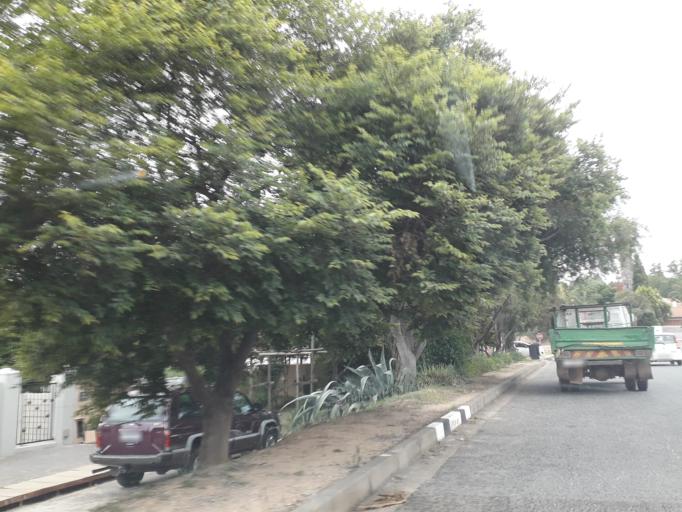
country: ZA
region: Gauteng
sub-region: City of Johannesburg Metropolitan Municipality
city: Roodepoort
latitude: -26.1054
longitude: 27.9455
